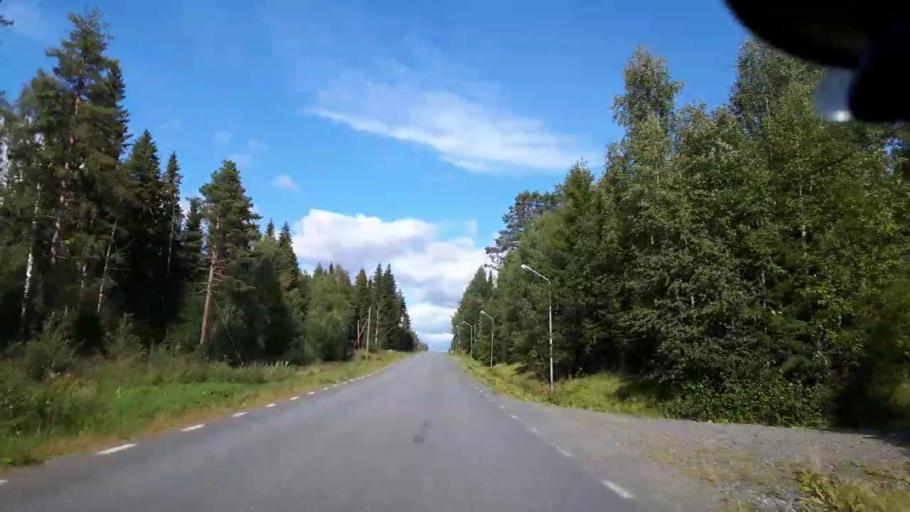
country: SE
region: Jaemtland
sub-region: Braecke Kommun
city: Braecke
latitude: 63.1819
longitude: 15.5554
